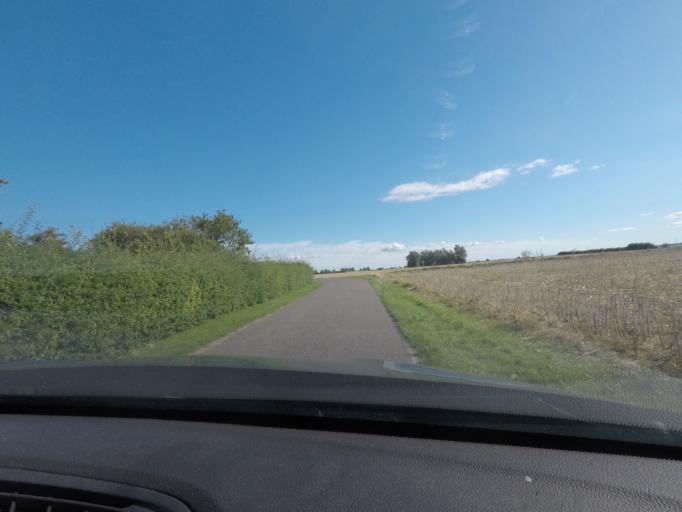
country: DK
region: Zealand
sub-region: Lolland Kommune
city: Maribo
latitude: 54.9718
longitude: 11.5236
